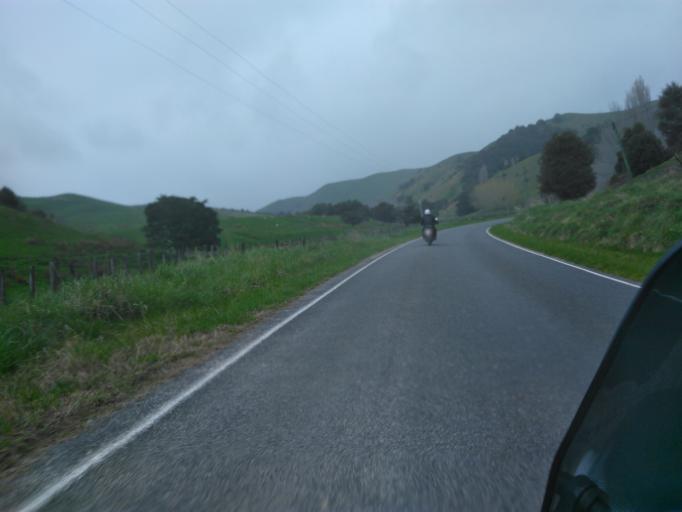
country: NZ
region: Gisborne
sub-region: Gisborne District
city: Gisborne
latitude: -38.6403
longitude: 177.7034
